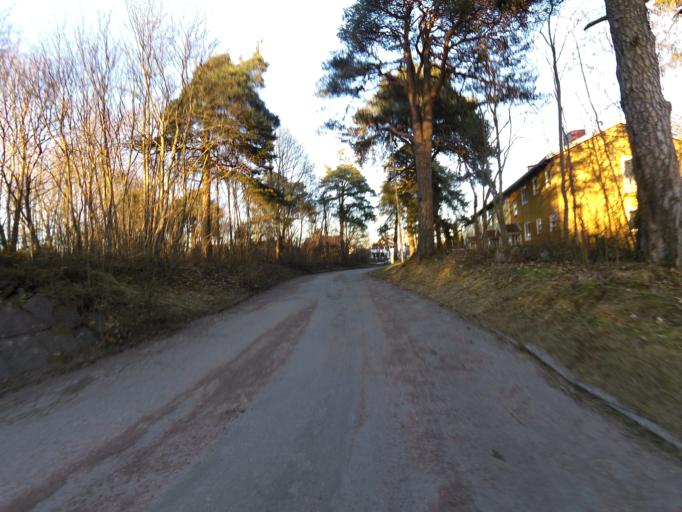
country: SE
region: Gaevleborg
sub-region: Gavle Kommun
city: Gavle
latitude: 60.6666
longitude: 17.1266
